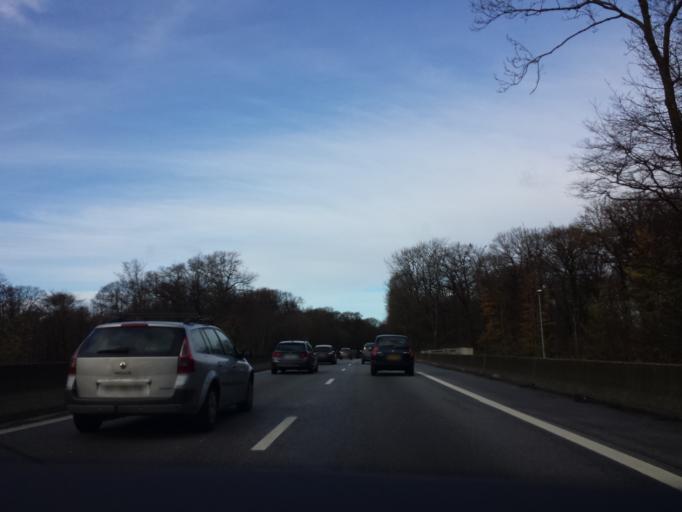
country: FR
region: Ile-de-France
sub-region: Departement des Yvelines
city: Saint-Nom-la-Breteche
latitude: 48.8664
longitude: 2.0353
